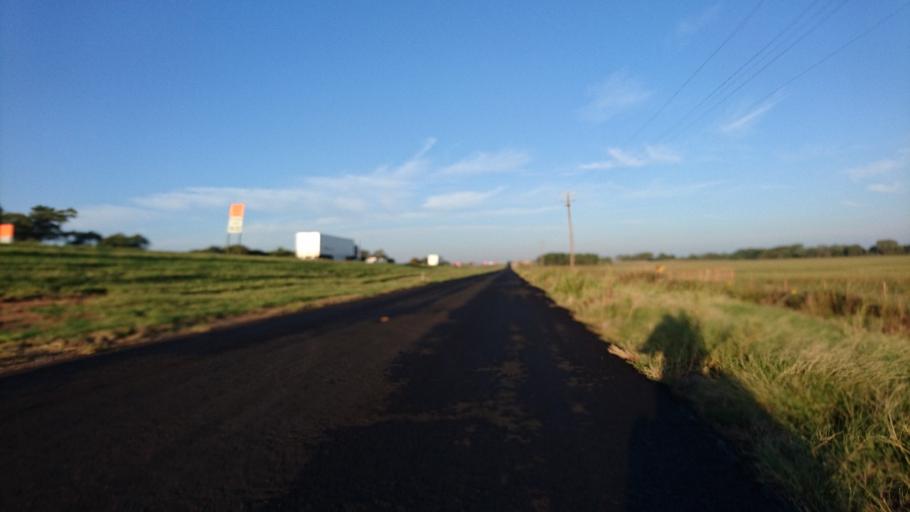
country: US
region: Oklahoma
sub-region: Beckham County
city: Sayre
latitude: 35.2624
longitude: -99.6859
